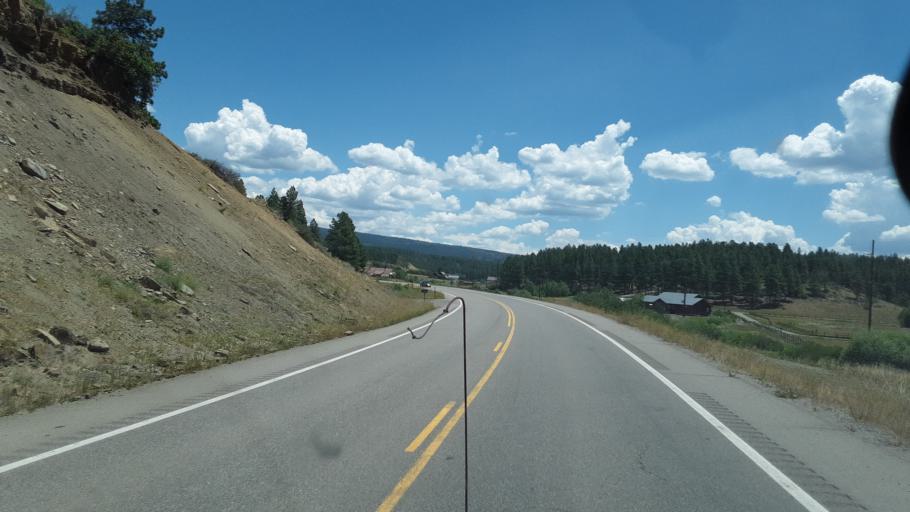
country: US
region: Colorado
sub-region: La Plata County
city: Bayfield
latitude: 37.2852
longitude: -107.5299
